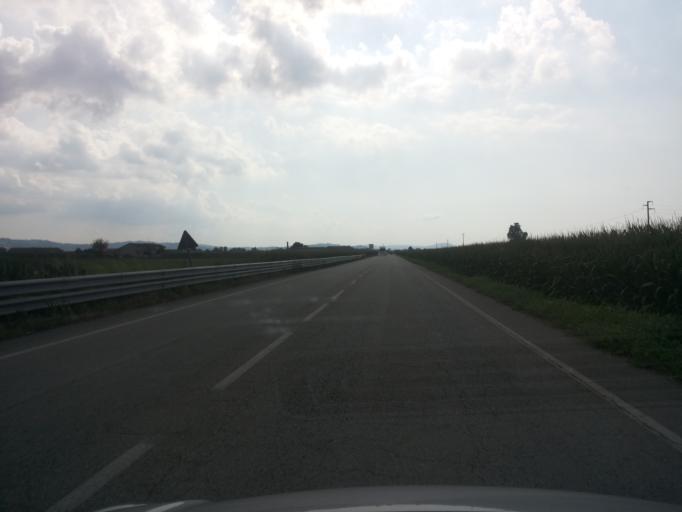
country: IT
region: Piedmont
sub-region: Provincia di Alessandria
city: Villanova Monferrato
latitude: 45.1614
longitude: 8.4763
